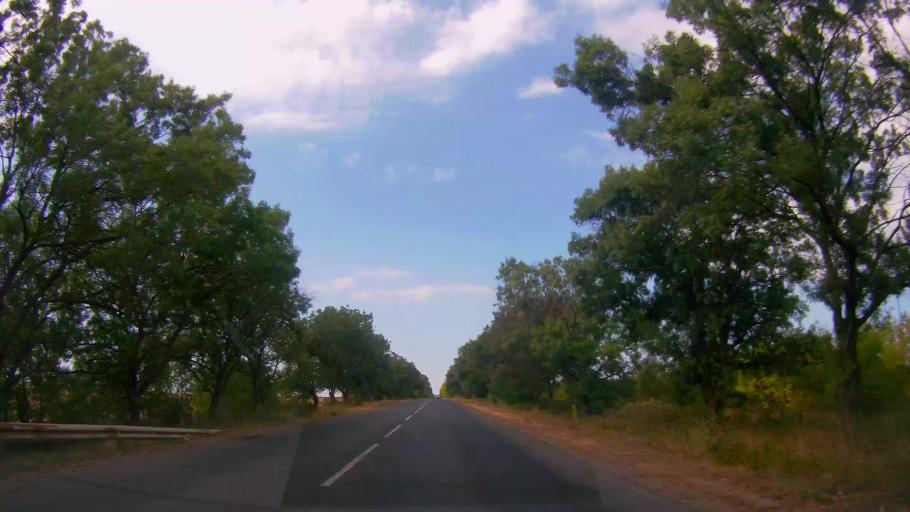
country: BG
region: Burgas
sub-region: Obshtina Aytos
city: Aytos
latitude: 42.6899
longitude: 27.1577
